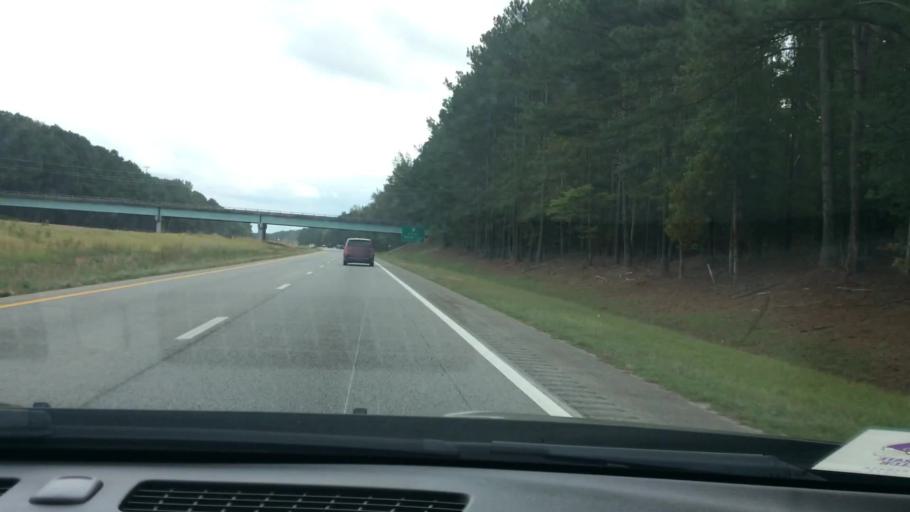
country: US
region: North Carolina
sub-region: Nash County
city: Spring Hope
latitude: 35.7898
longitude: -78.1402
